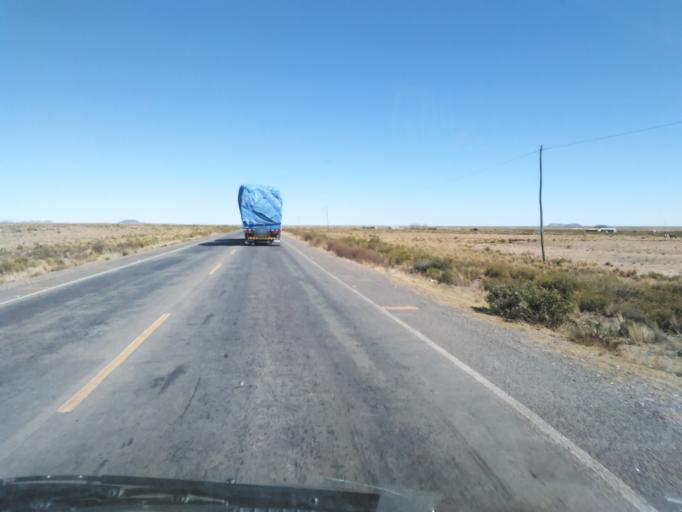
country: BO
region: Oruro
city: Machacamarca
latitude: -18.0848
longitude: -67.0090
